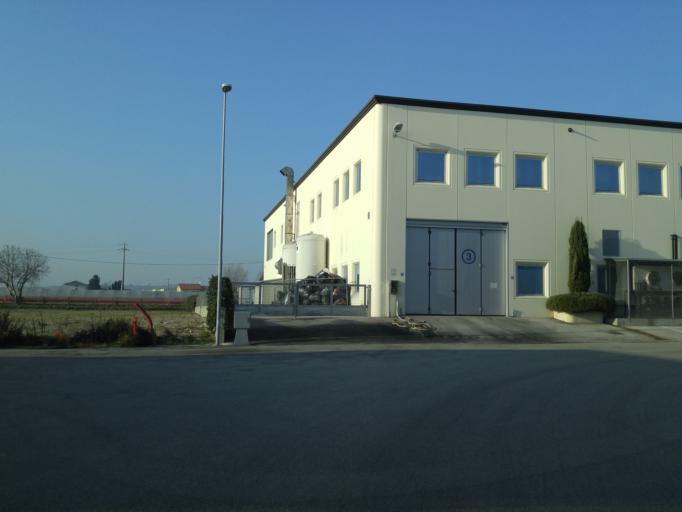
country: IT
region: The Marches
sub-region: Provincia di Pesaro e Urbino
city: Lucrezia
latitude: 43.7703
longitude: 12.9541
